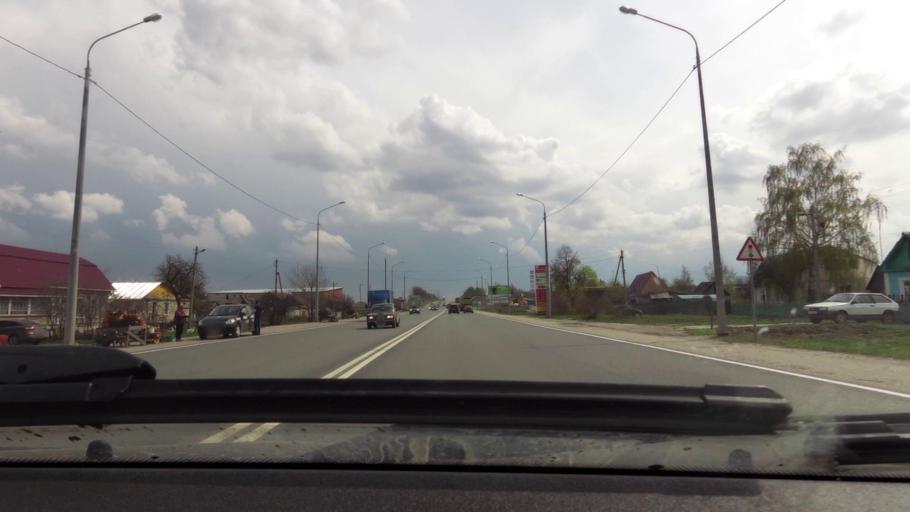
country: RU
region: Rjazan
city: Bagramovo
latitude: 54.7306
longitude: 39.4633
